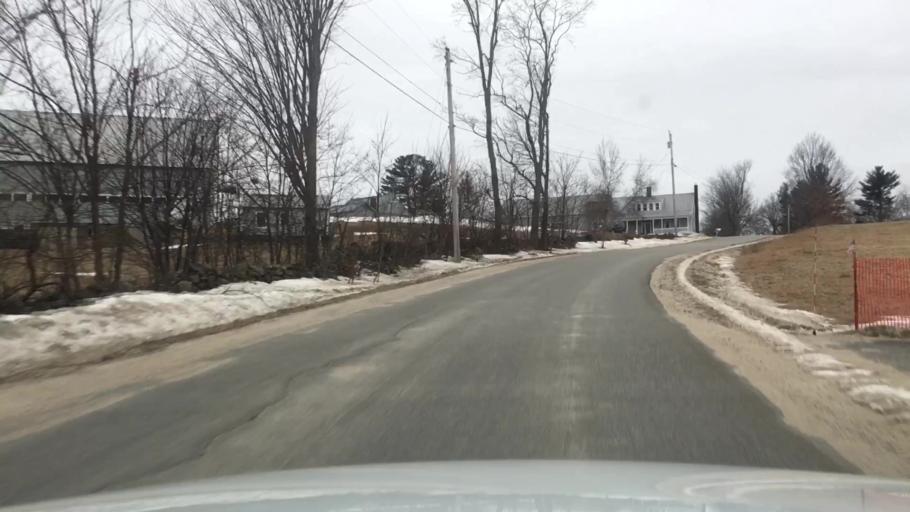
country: US
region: Maine
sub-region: York County
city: Springvale
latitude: 43.4984
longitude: -70.8186
